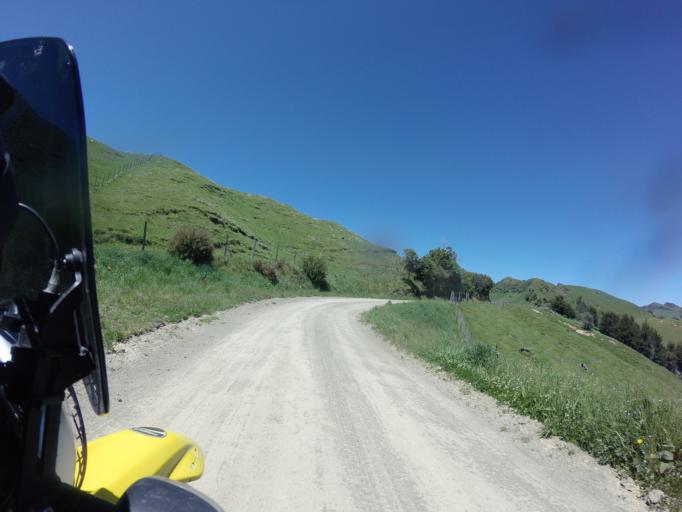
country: NZ
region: Bay of Plenty
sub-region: Opotiki District
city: Opotiki
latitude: -38.4011
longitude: 177.4567
